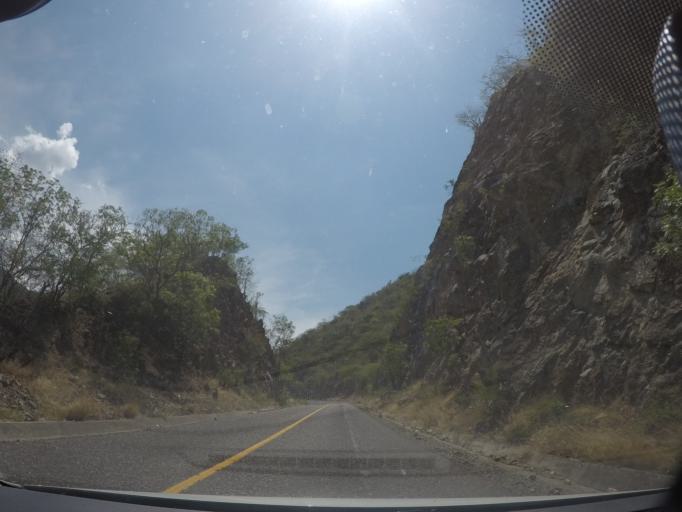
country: MX
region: Oaxaca
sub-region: San Pedro Quiatoni
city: San Pedro Quiatoni
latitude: 16.6636
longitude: -96.1039
